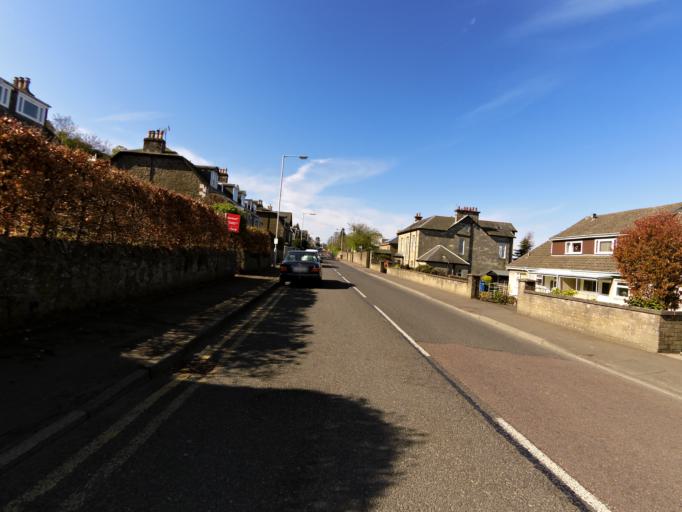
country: GB
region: Scotland
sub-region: Fife
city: Newport-On-Tay
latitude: 56.4285
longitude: -2.9712
